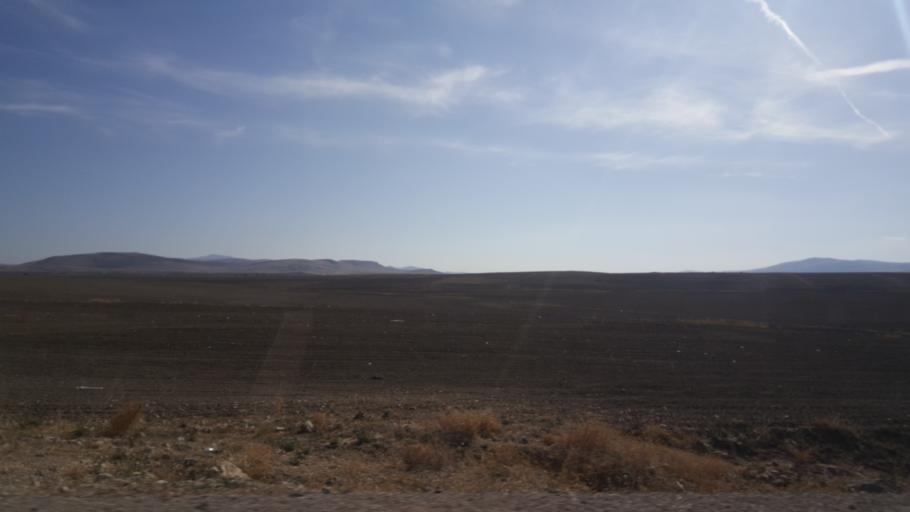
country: TR
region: Ankara
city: Yenice
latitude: 39.3809
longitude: 32.7823
